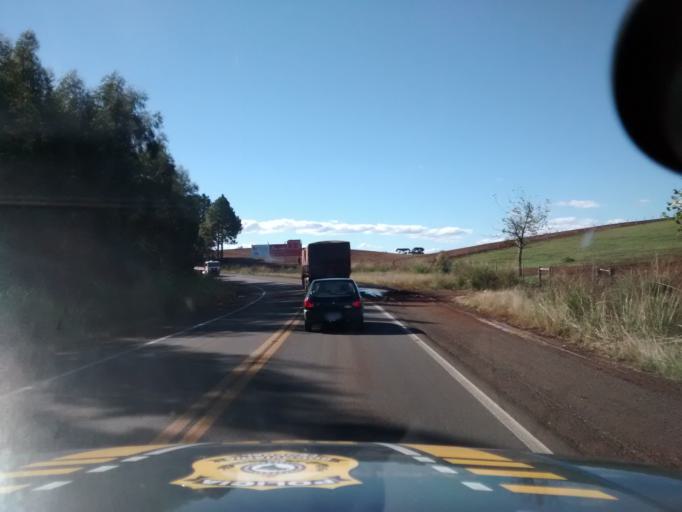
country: BR
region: Rio Grande do Sul
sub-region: Lagoa Vermelha
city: Lagoa Vermelha
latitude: -28.2767
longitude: -51.4677
